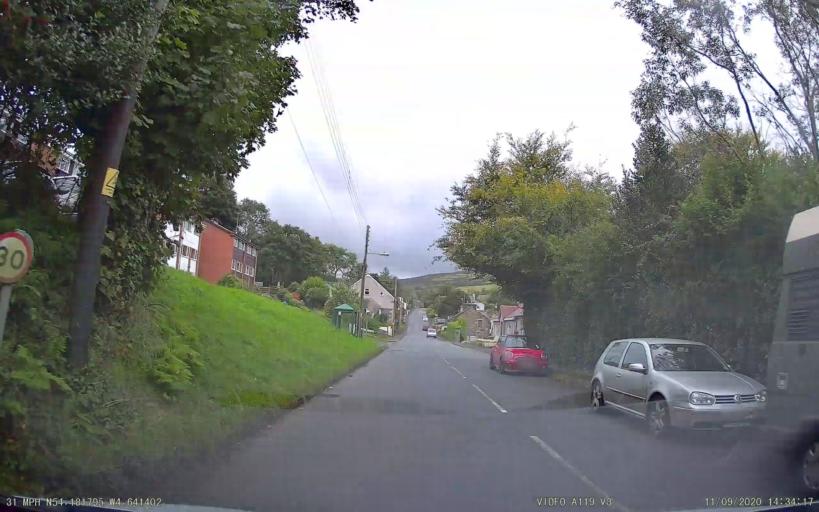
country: IM
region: Castletown
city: Castletown
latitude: 54.1818
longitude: -4.6414
